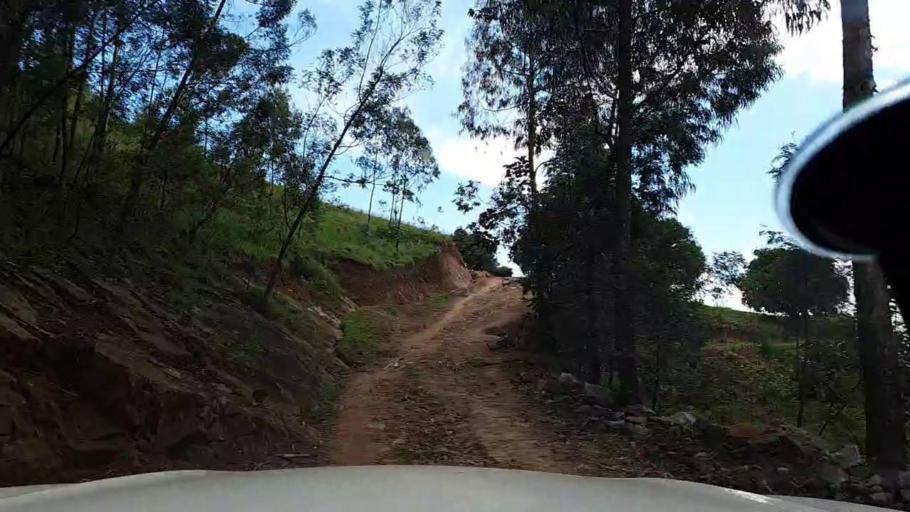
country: RW
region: Southern Province
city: Gitarama
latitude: -1.8076
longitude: 29.8009
